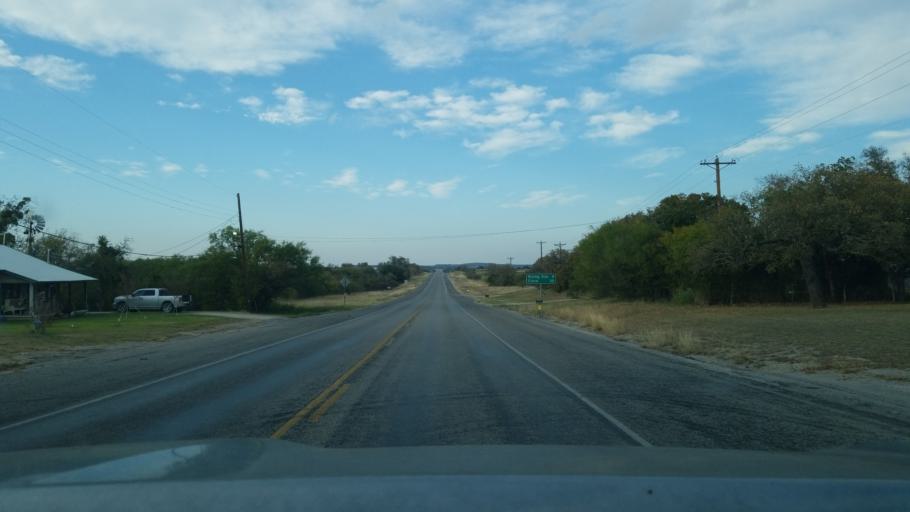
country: US
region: Texas
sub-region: Brown County
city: Lake Brownwood
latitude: 31.9826
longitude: -98.9207
